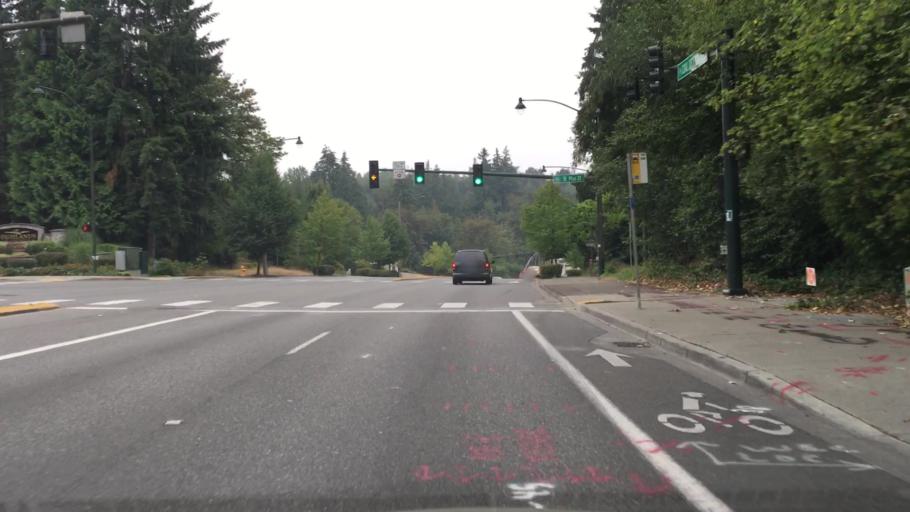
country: US
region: Washington
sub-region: King County
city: Newcastle
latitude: 47.5206
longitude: -122.1591
